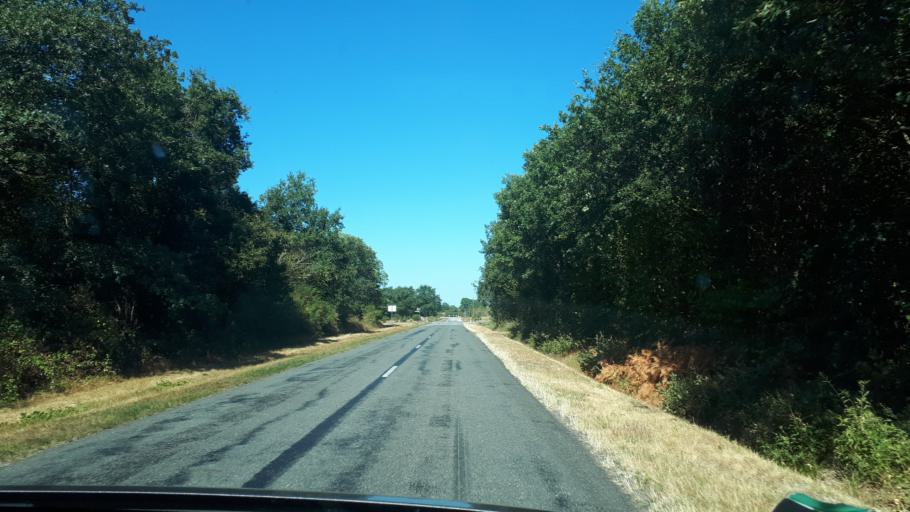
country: FR
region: Centre
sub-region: Departement du Loiret
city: Coullons
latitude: 47.6362
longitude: 2.4504
